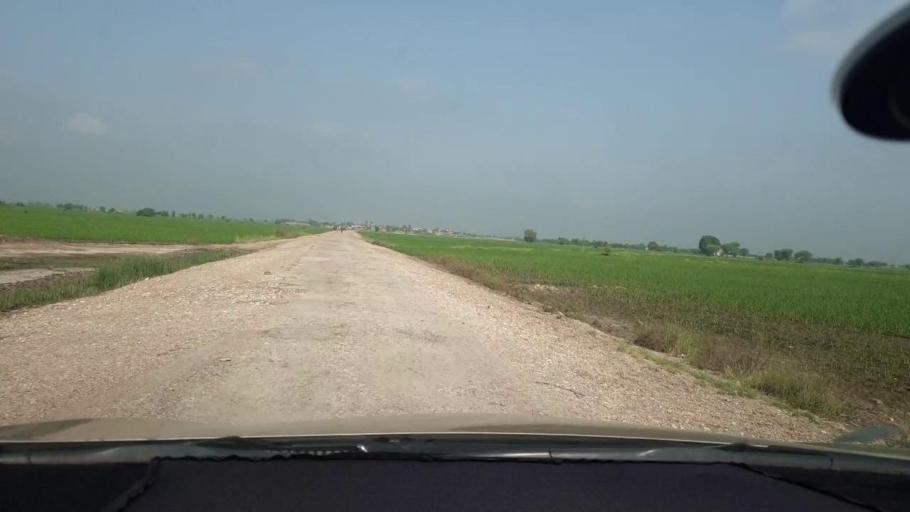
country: PK
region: Sindh
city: Kambar
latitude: 27.5379
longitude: 68.0566
